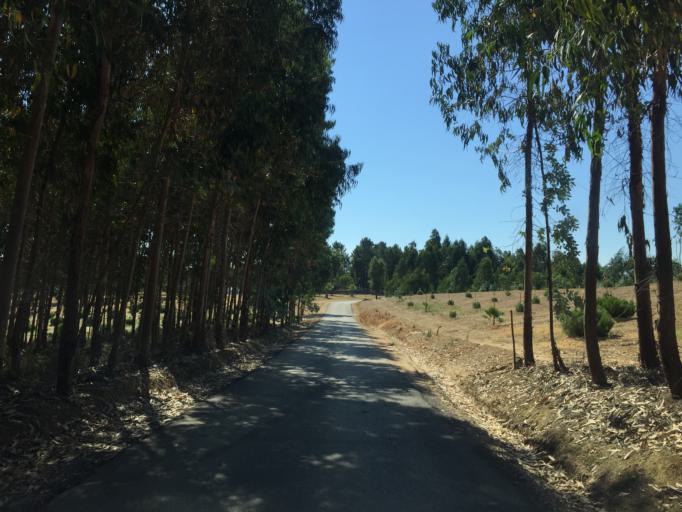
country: PT
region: Santarem
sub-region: Ferreira do Zezere
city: Ferreira do Zezere
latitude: 39.5919
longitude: -8.2853
